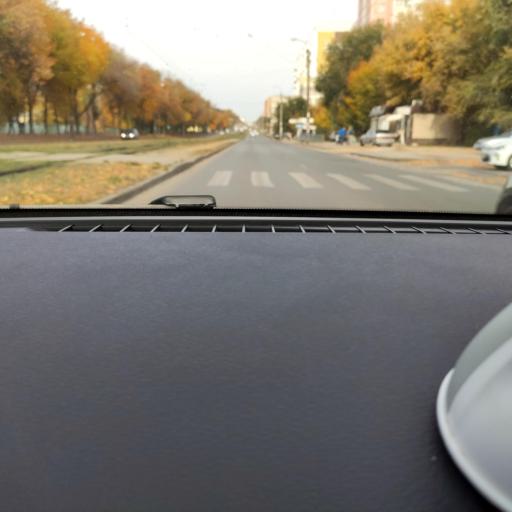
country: RU
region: Samara
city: Samara
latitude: 53.2259
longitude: 50.2313
